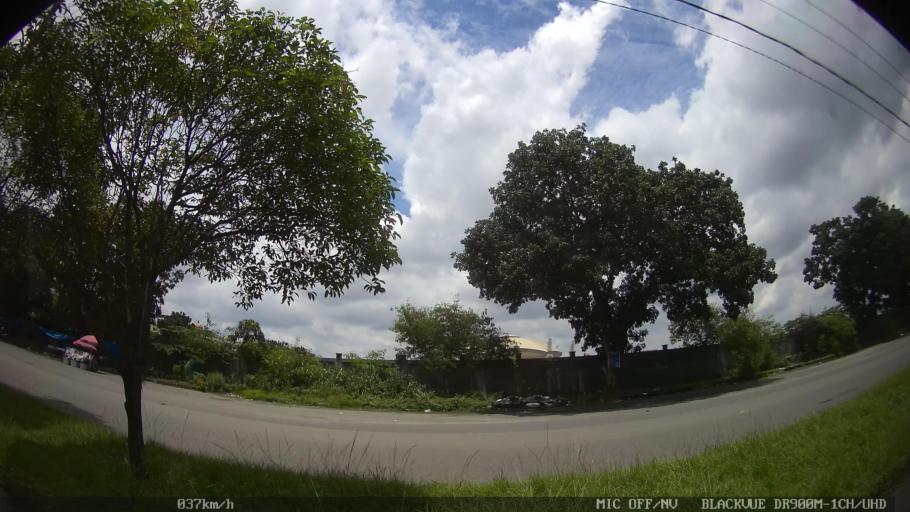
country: ID
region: North Sumatra
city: Medan
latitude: 3.6069
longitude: 98.7120
